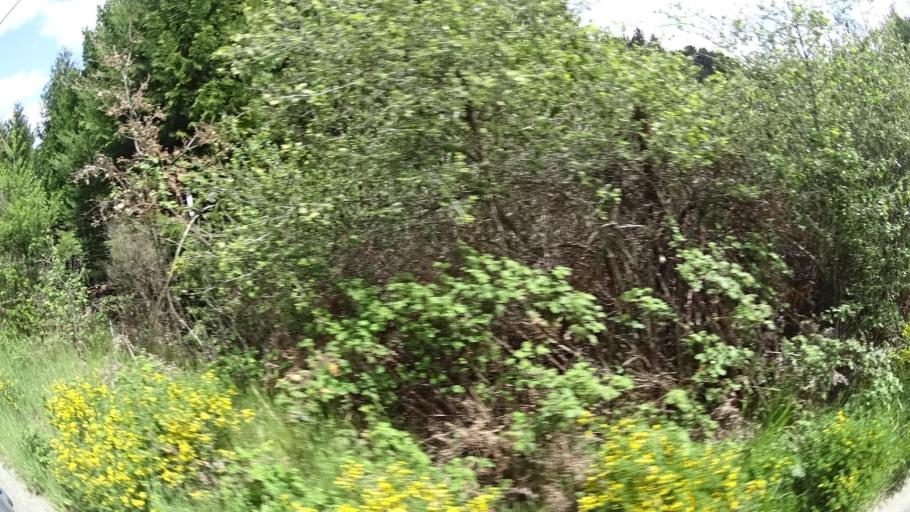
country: US
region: California
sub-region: Humboldt County
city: Redway
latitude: 40.0653
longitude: -123.9629
